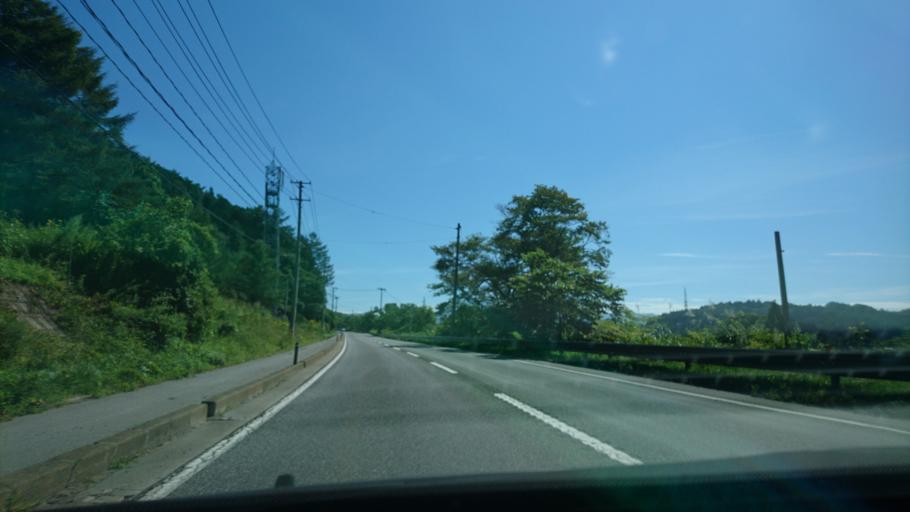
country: JP
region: Iwate
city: Tono
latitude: 39.3322
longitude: 141.5143
